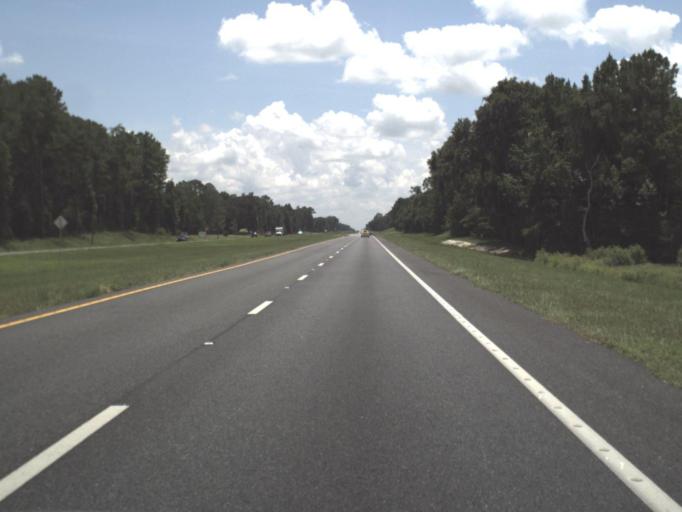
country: US
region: Florida
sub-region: Levy County
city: Williston
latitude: 29.3696
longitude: -82.4130
